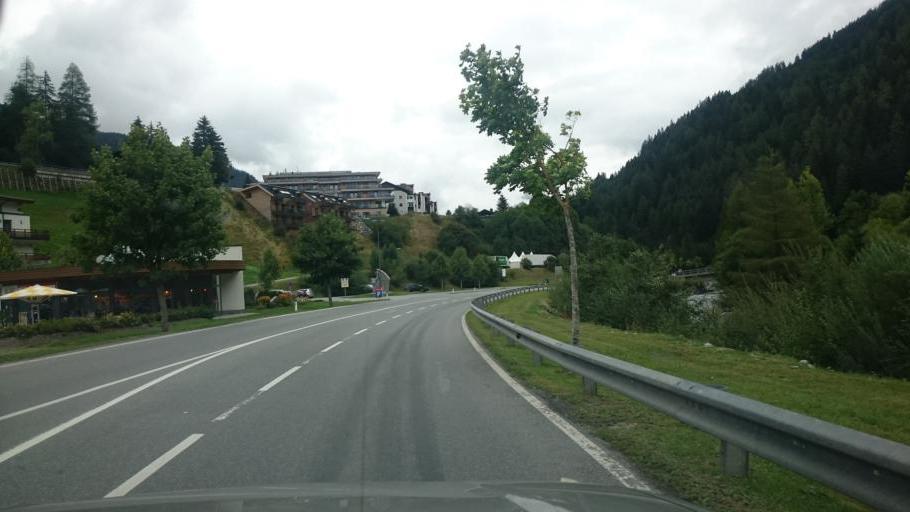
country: AT
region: Tyrol
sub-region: Politischer Bezirk Landeck
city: Sankt Anton am Arlberg
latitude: 47.1354
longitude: 10.2767
